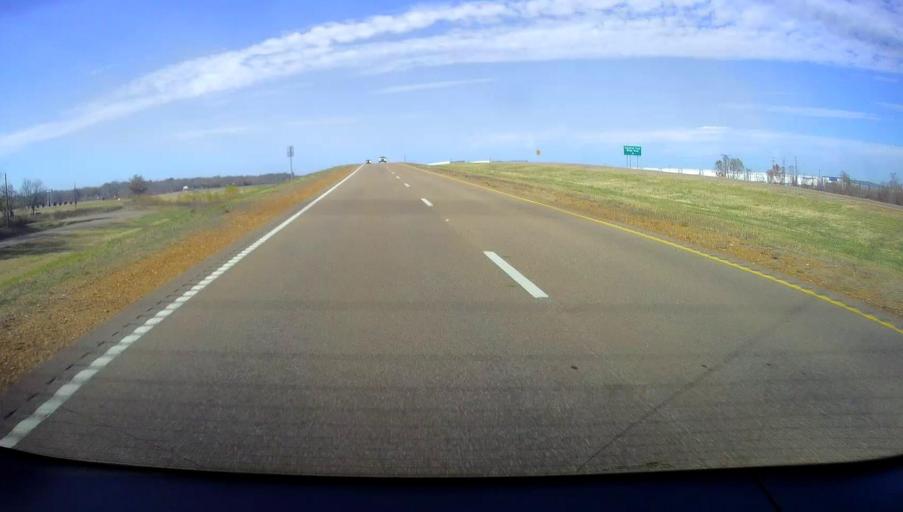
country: US
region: Tennessee
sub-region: Fayette County
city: Piperton
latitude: 34.9845
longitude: -89.5932
